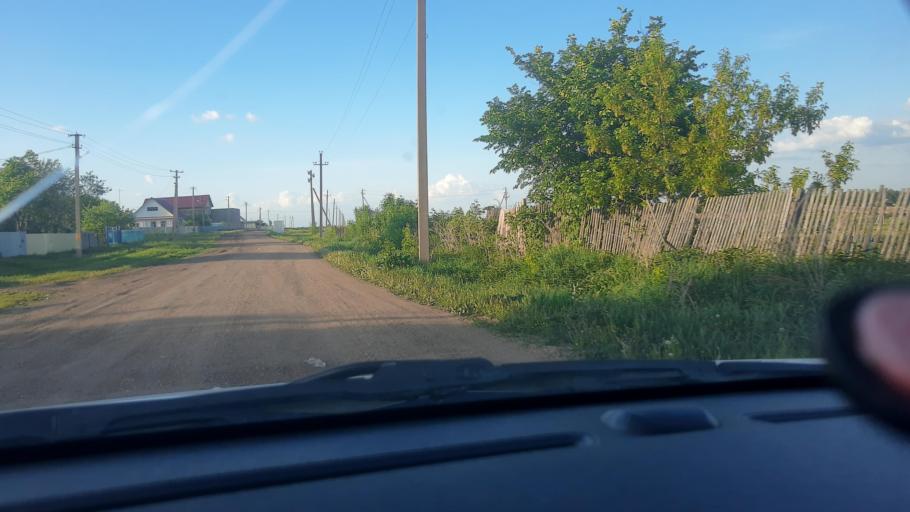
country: RU
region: Bashkortostan
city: Karmaskaly
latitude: 54.3824
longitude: 55.9395
